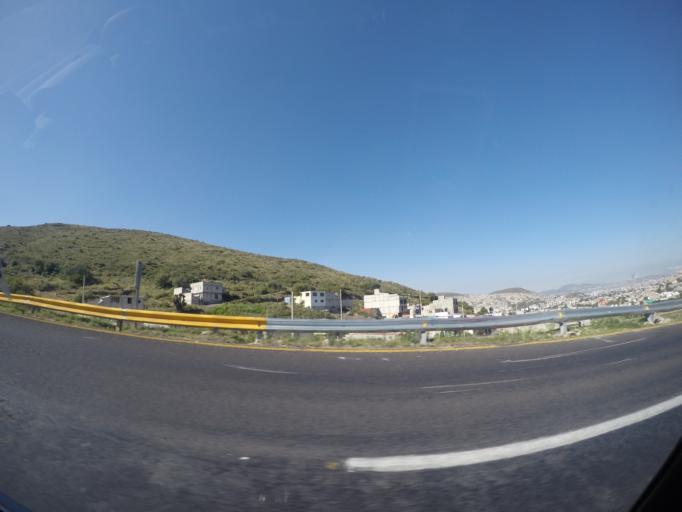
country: MX
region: Hidalgo
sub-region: Mineral de la Reforma
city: Rio de la Soledad
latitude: 20.1188
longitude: -98.7079
